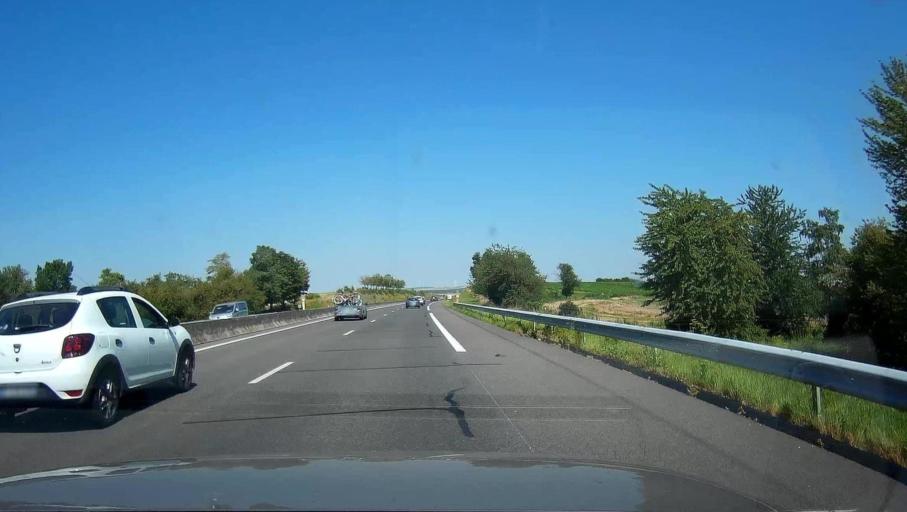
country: FR
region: Champagne-Ardenne
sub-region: Departement de l'Aube
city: Arcis-sur-Aube
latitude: 48.4958
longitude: 4.1650
